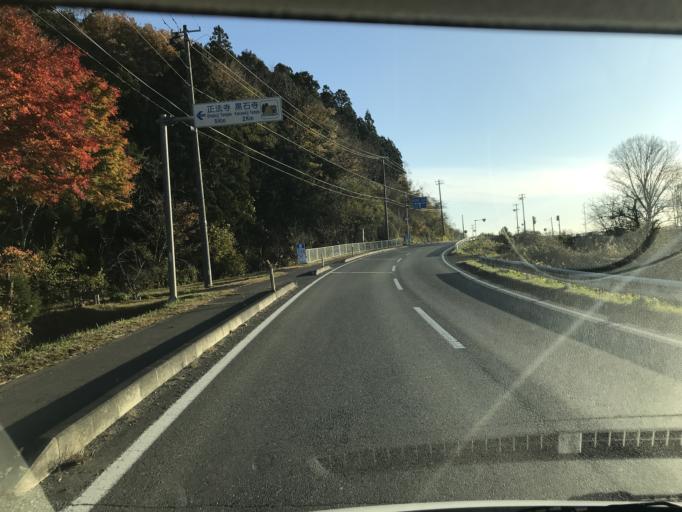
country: JP
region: Iwate
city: Mizusawa
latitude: 39.0951
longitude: 141.1910
